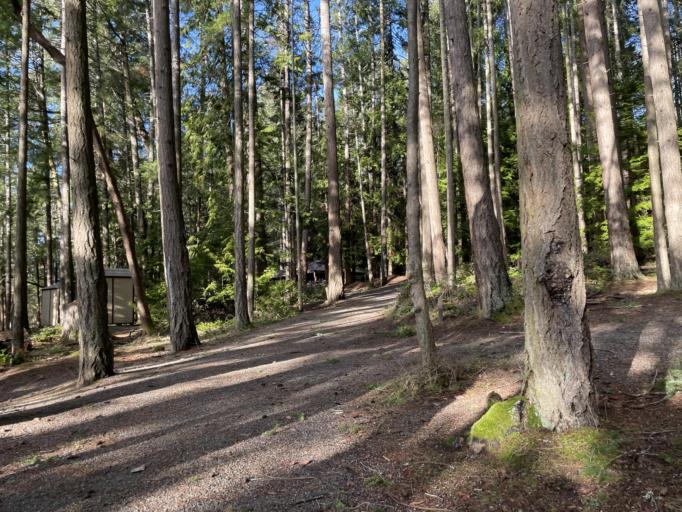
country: CA
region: British Columbia
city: North Saanich
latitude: 48.8975
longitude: -123.4053
